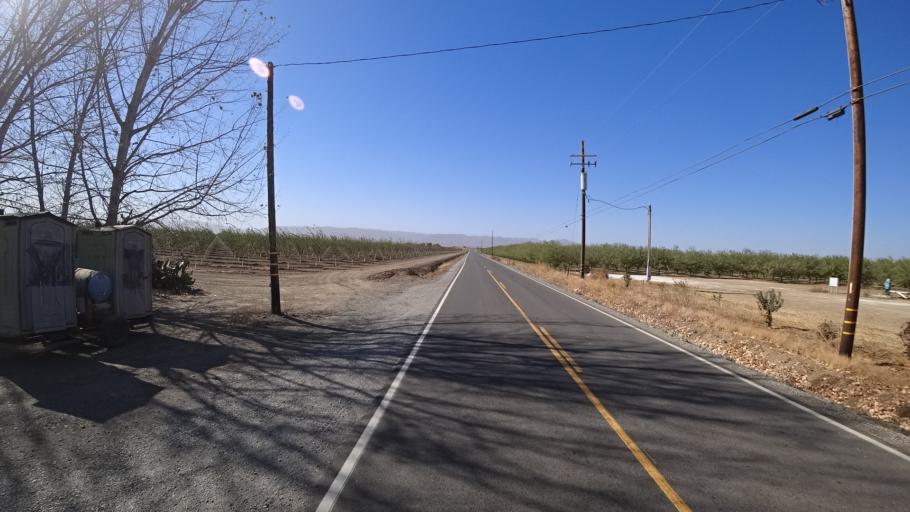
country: US
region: California
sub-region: Yolo County
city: Winters
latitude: 38.5840
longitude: -121.9443
